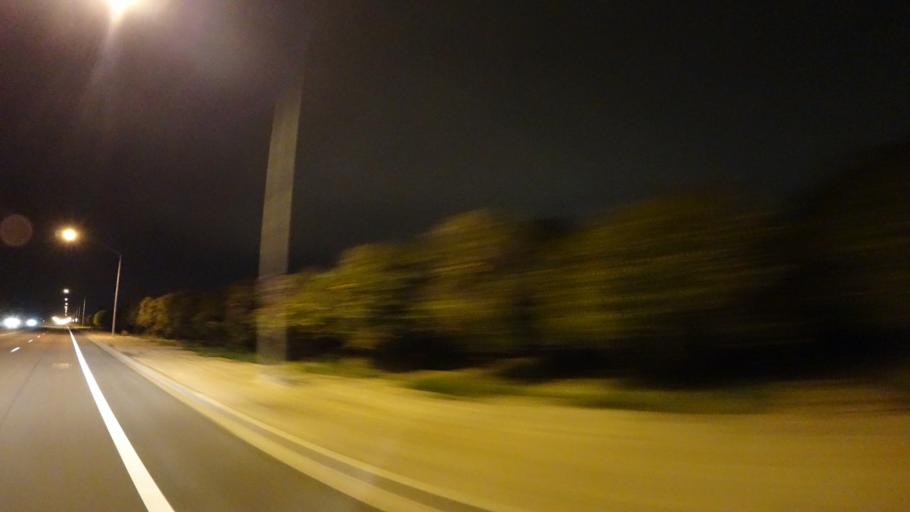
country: US
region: Arizona
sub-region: Maricopa County
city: Mesa
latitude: 33.4655
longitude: -111.7360
